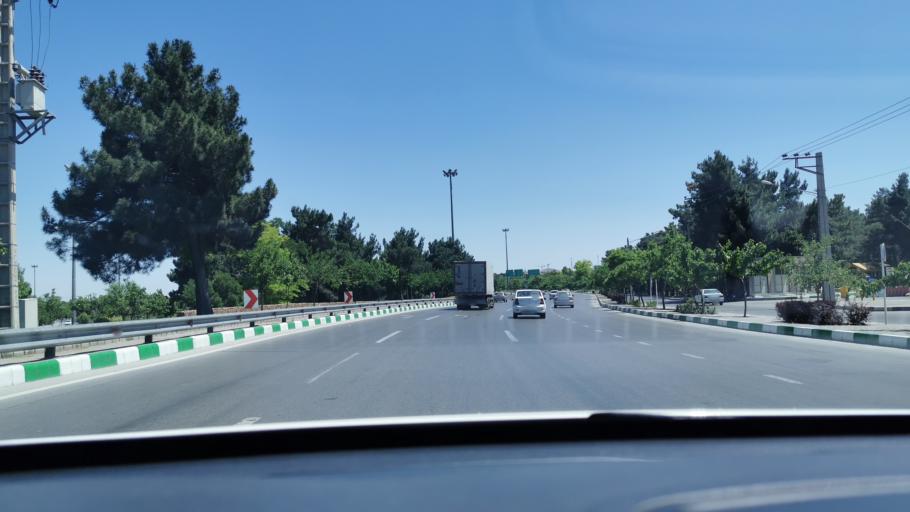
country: IR
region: Razavi Khorasan
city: Mashhad
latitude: 36.2523
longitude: 59.6061
